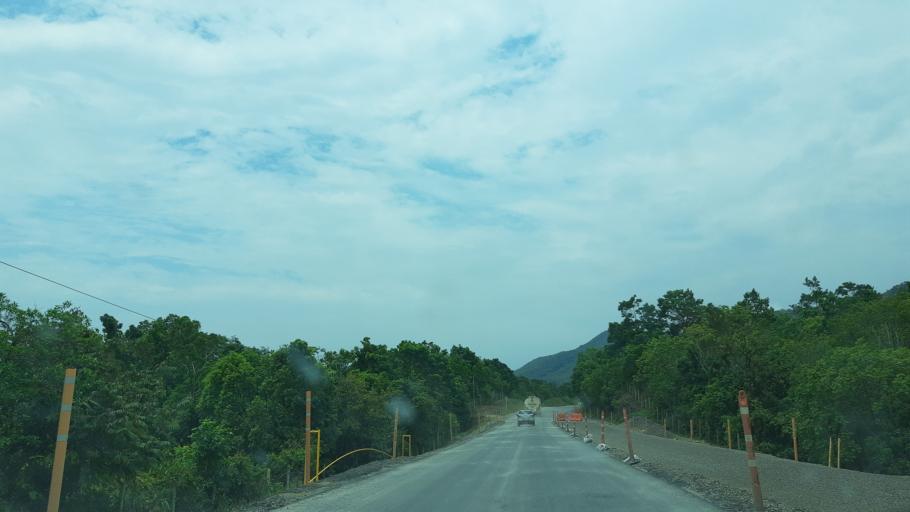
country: CO
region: Casanare
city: Sabanalarga
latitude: 4.7721
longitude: -73.0039
